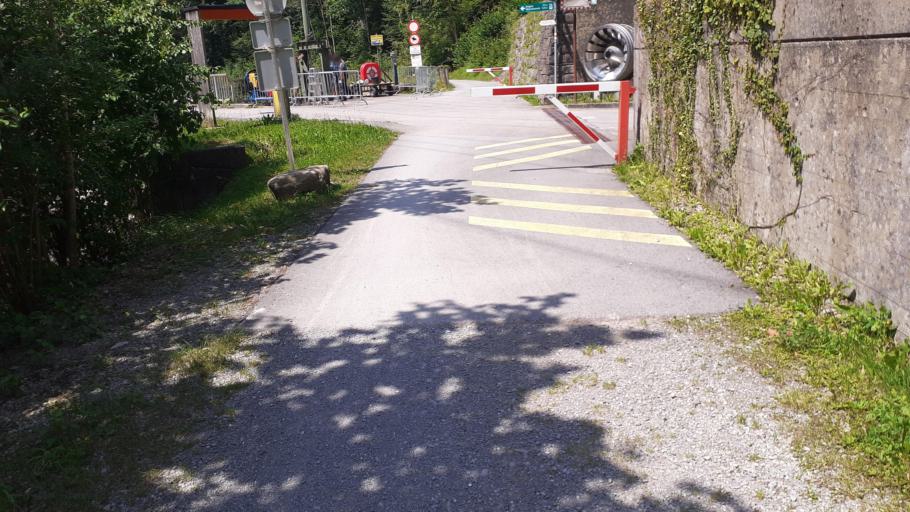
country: AT
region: Vorarlberg
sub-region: Politischer Bezirk Bregenz
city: Doren
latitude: 47.4703
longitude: 9.8636
